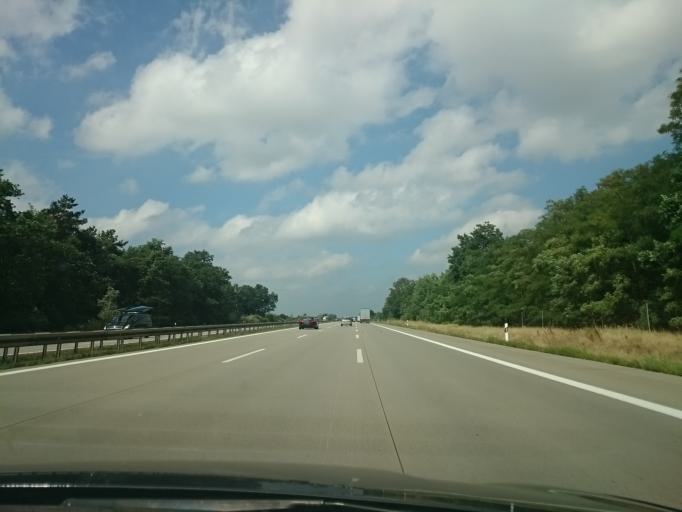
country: DE
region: Brandenburg
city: Ahrensfelde
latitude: 52.5839
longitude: 13.6315
